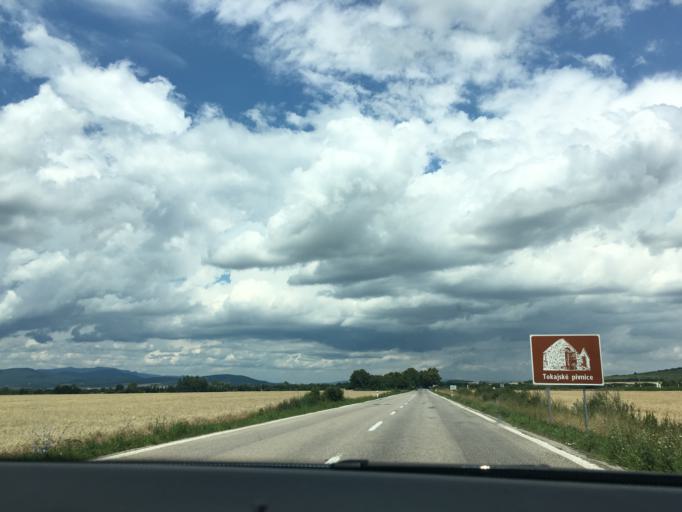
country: HU
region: Borsod-Abauj-Zemplen
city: Satoraljaujhely
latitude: 48.4417
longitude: 21.6546
